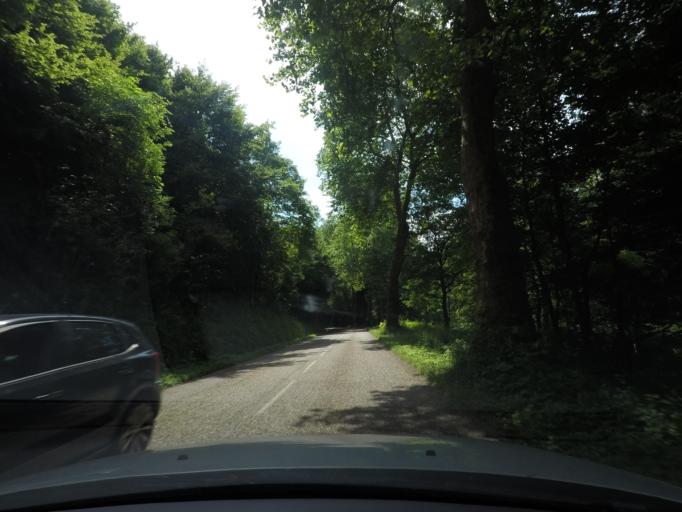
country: FR
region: Lorraine
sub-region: Departement de la Moselle
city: Phalsbourg
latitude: 48.8147
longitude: 7.2872
